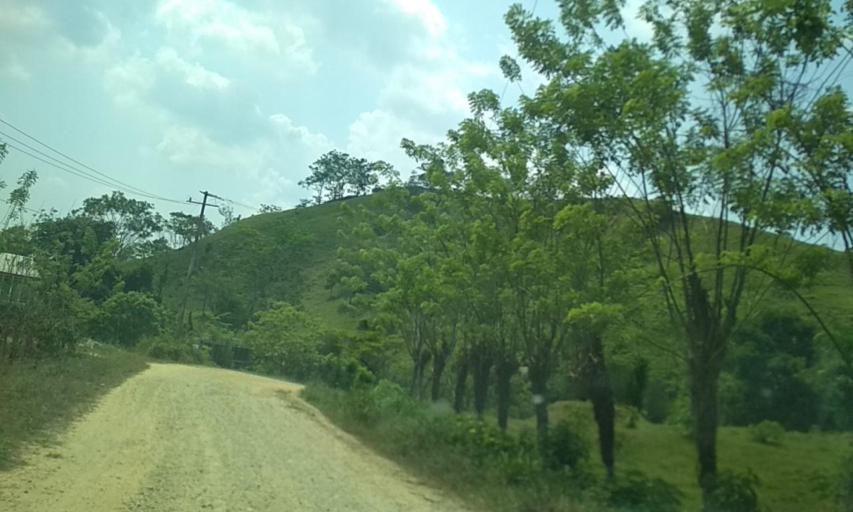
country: MX
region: Chiapas
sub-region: Tecpatan
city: Raudales Malpaso
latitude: 17.3497
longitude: -93.9646
